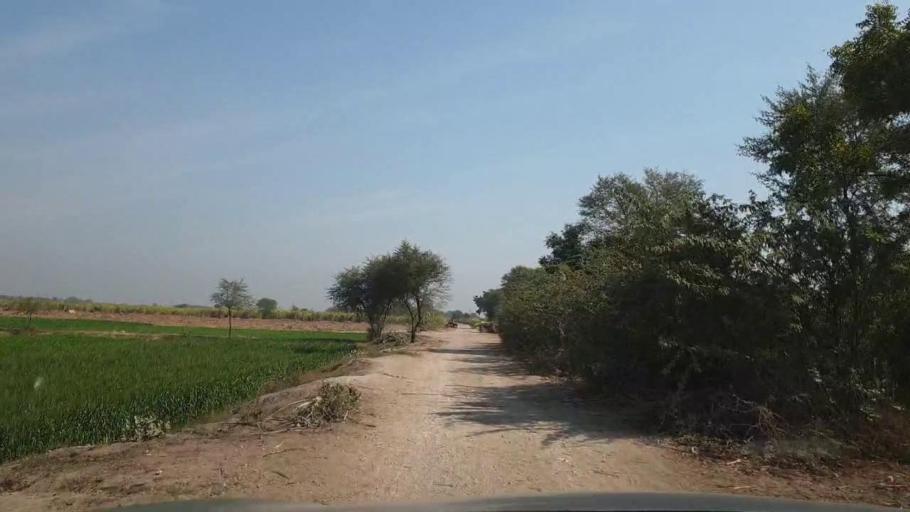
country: PK
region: Sindh
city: Tando Adam
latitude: 25.6481
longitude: 68.7339
